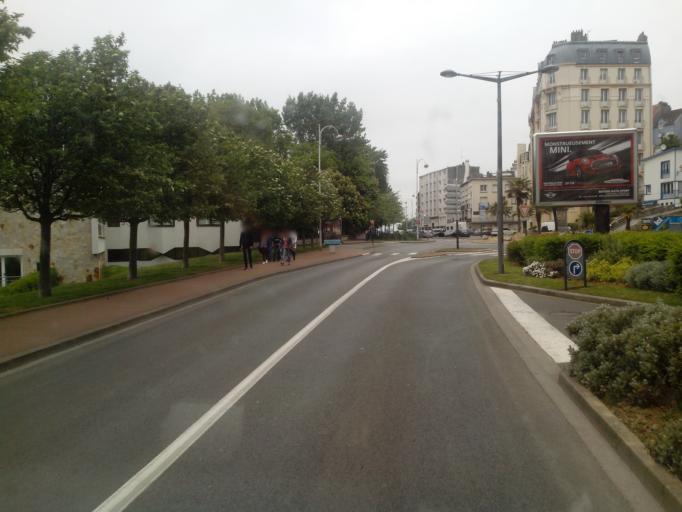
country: FR
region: Nord-Pas-de-Calais
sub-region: Departement du Pas-de-Calais
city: Saint-Martin-Boulogne
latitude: 50.7284
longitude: 1.5982
